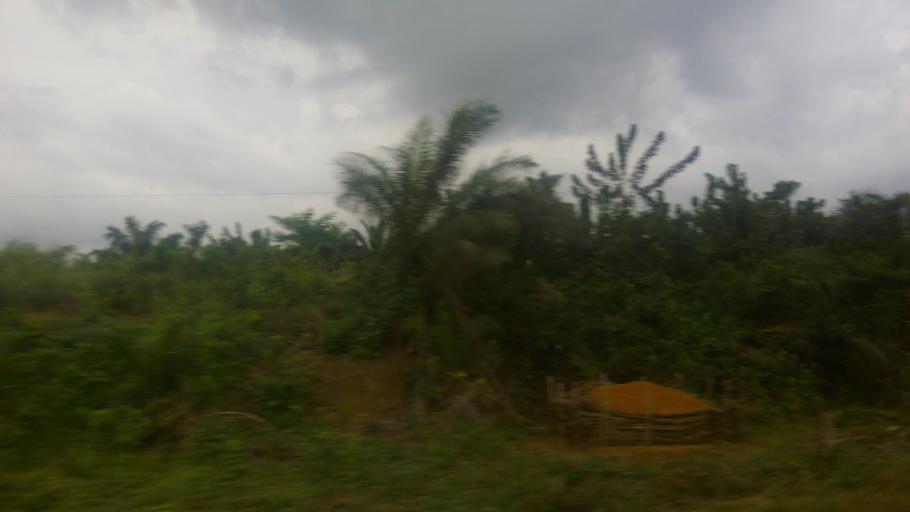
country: GH
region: Western
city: Takoradi
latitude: 4.8970
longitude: -1.9323
